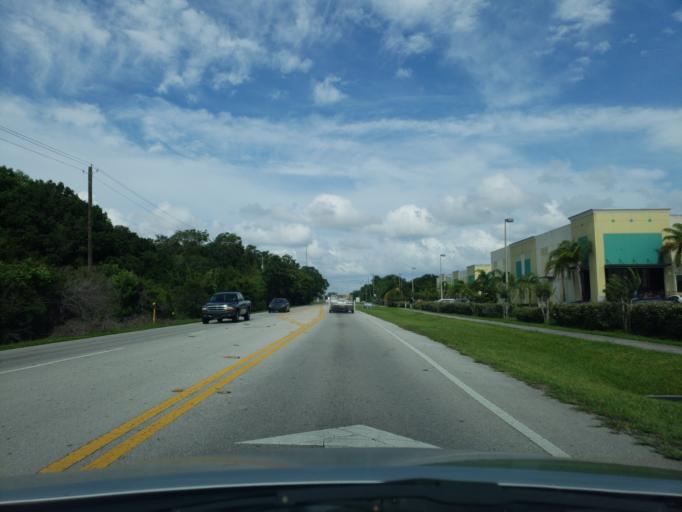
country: US
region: Florida
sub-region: Hillsborough County
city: Egypt Lake-Leto
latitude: 28.0108
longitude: -82.5281
